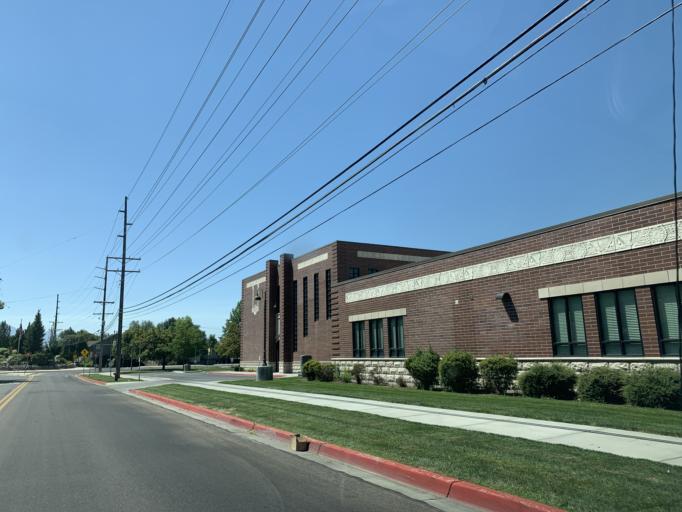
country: US
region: Utah
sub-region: Utah County
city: Provo
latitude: 40.2346
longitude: -111.6466
